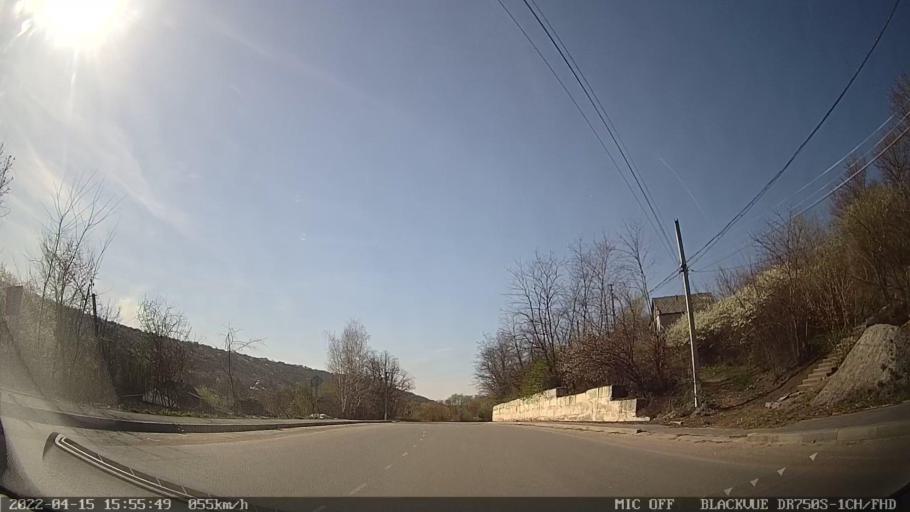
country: MD
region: Raionul Ocnita
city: Otaci
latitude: 48.4006
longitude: 27.8794
